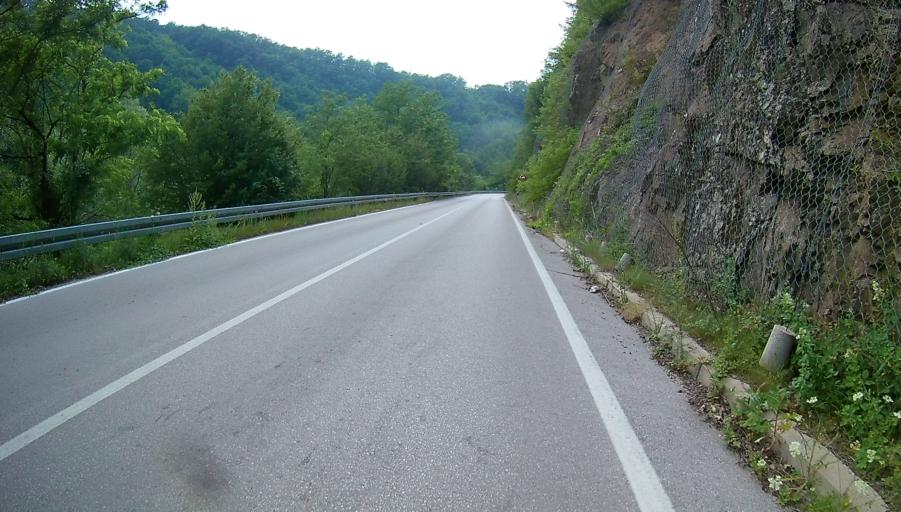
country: RS
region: Central Serbia
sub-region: Nisavski Okrug
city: Gadzin Han
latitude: 43.1802
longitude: 22.0320
